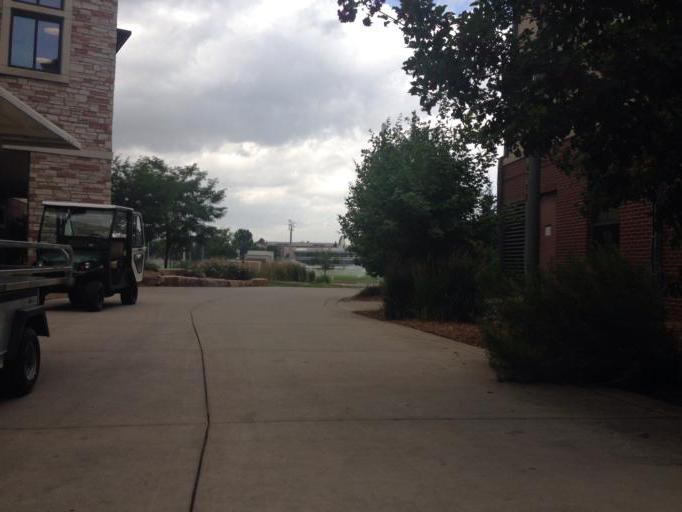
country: US
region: Colorado
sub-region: Larimer County
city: Fort Collins
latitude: 40.5718
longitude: -105.0908
